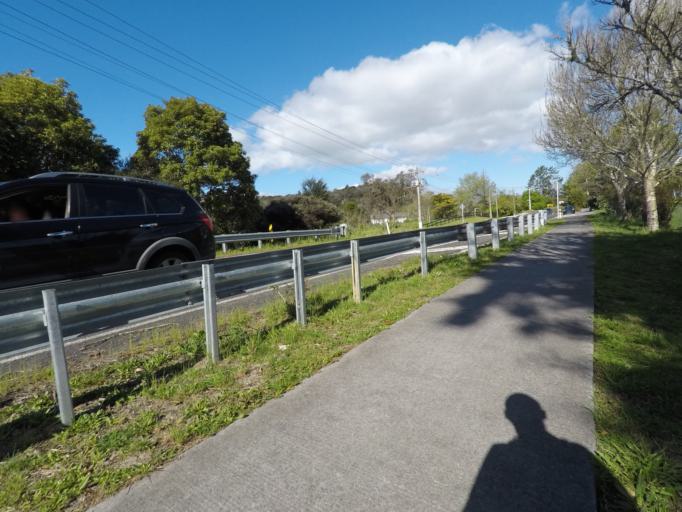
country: NZ
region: Auckland
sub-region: Auckland
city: Rosebank
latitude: -36.8542
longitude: 174.6018
